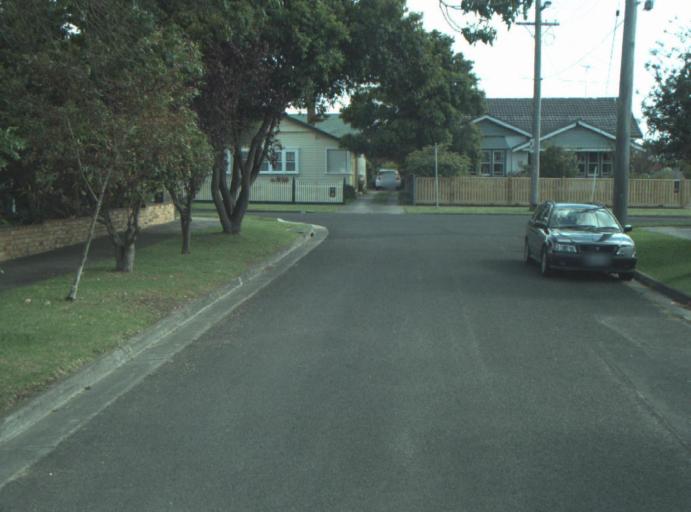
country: AU
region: Victoria
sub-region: Greater Geelong
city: Breakwater
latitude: -38.1763
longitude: 144.3393
